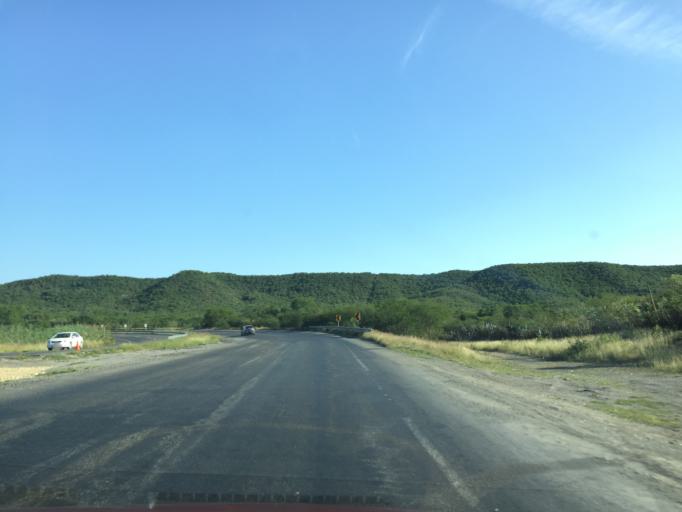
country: MX
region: Nuevo Leon
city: Montemorelos
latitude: 25.1330
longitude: -99.8281
